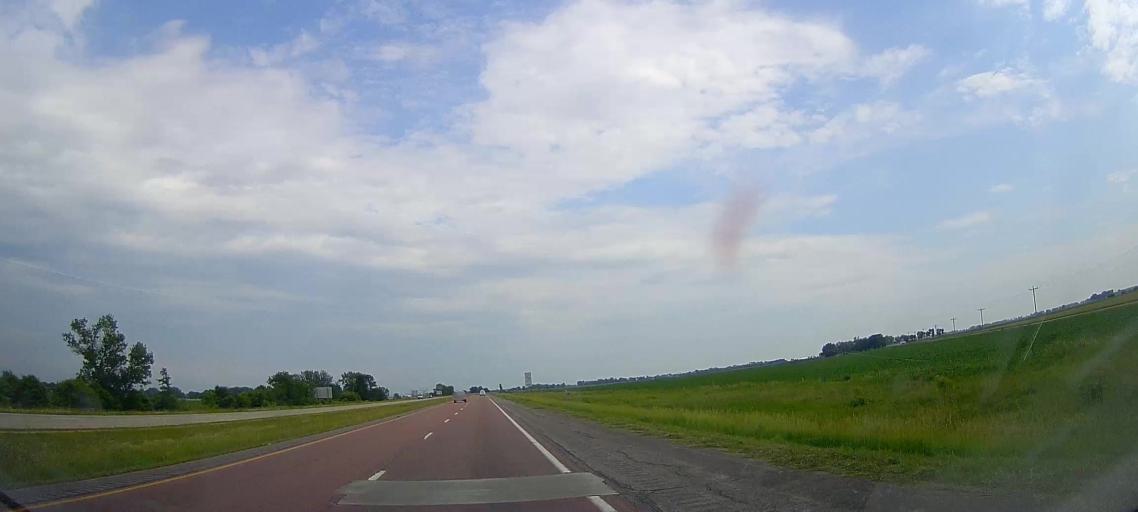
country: US
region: Iowa
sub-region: Monona County
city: Onawa
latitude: 42.0185
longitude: -96.1260
